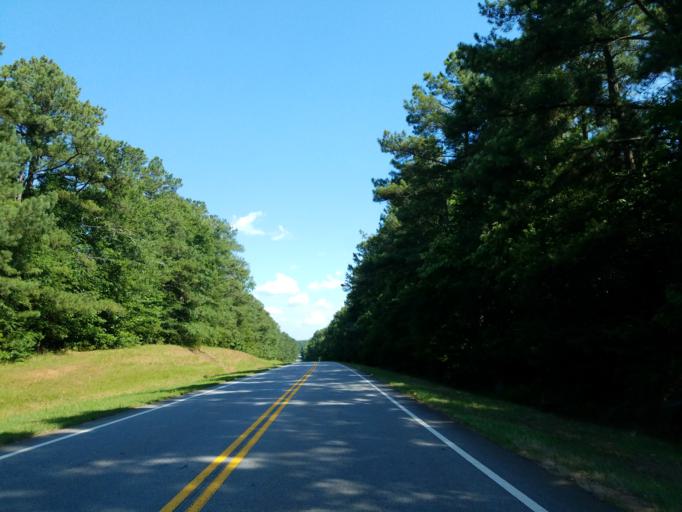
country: US
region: Georgia
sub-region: Crawford County
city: Roberta
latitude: 32.8470
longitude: -84.0724
